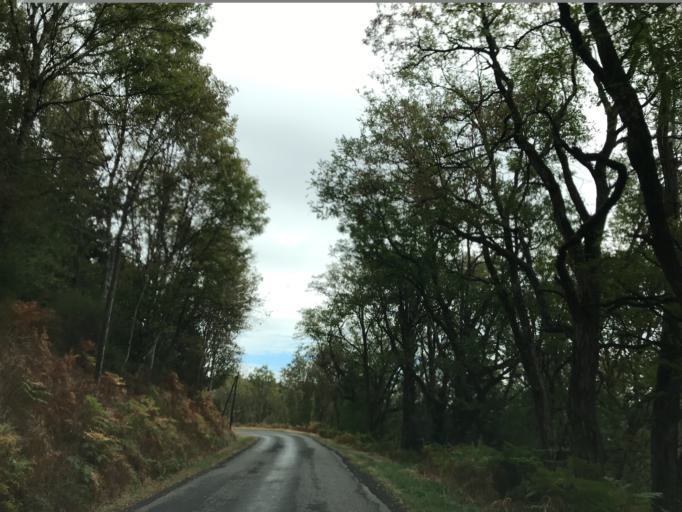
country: FR
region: Auvergne
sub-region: Departement du Puy-de-Dome
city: Thiers
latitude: 45.8351
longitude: 3.5699
